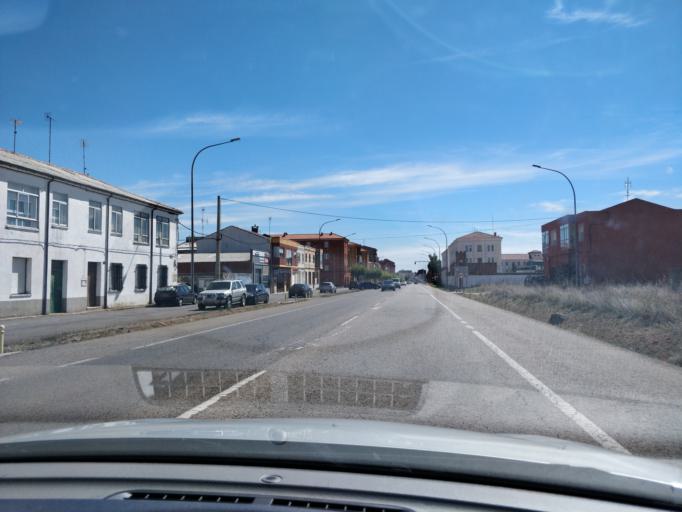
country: ES
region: Castille and Leon
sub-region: Provincia de Leon
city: Astorga
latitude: 42.4634
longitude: -6.0707
